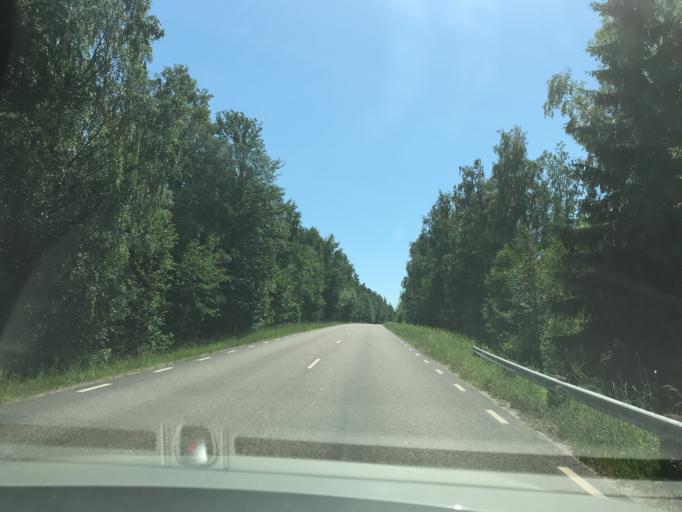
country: SE
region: Vaestra Goetaland
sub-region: Gotene Kommun
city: Goetene
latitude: 58.6121
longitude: 13.4017
